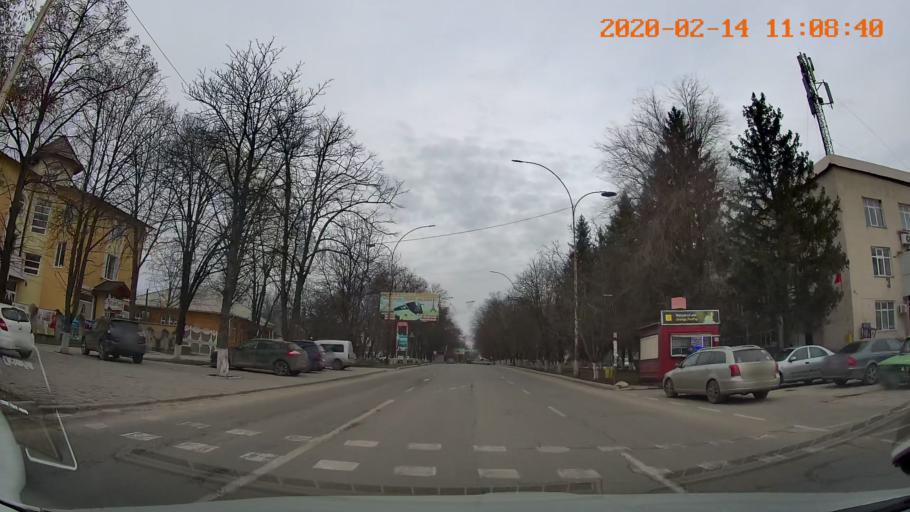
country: MD
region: Raionul Edinet
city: Edinet
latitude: 48.1733
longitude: 27.3002
